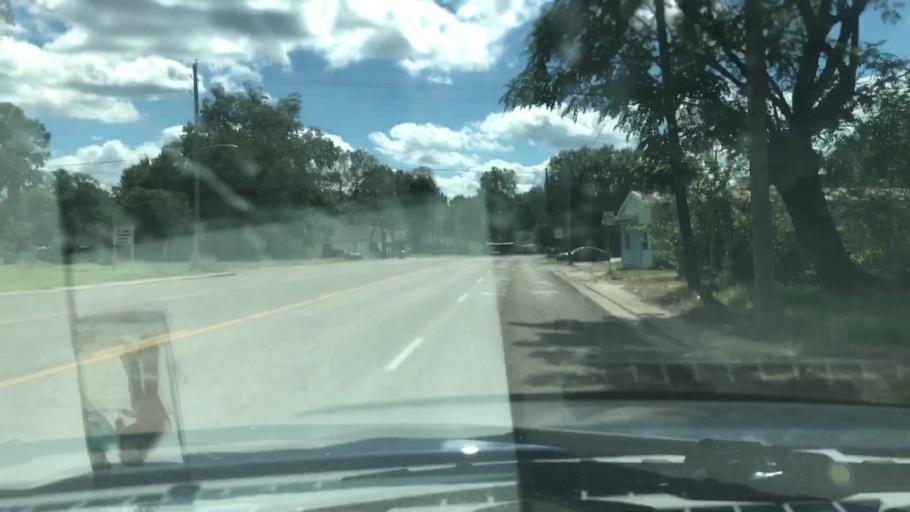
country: US
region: Texas
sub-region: Bowie County
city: Texarkana
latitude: 33.4077
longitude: -94.0607
